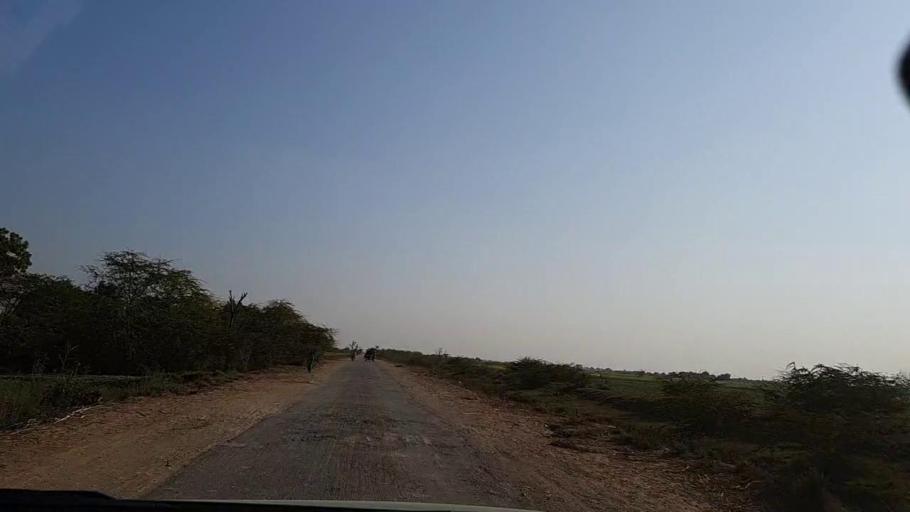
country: PK
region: Sindh
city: Tando Ghulam Ali
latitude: 25.2175
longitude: 68.9461
